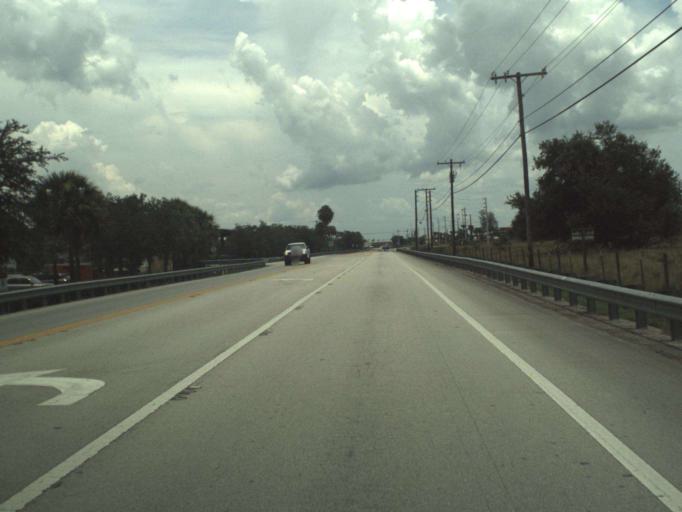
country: US
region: Florida
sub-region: Saint Lucie County
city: Lakewood Park
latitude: 27.4410
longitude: -80.3990
